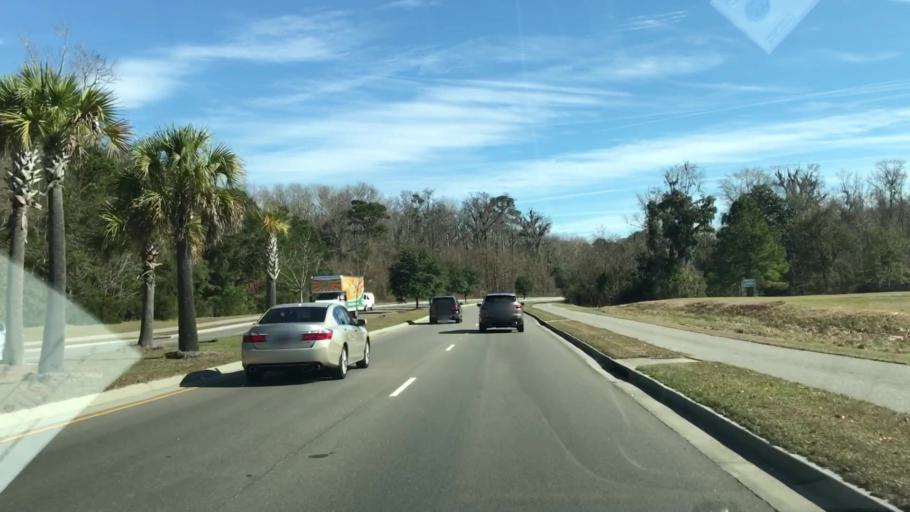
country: US
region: South Carolina
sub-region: Beaufort County
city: Bluffton
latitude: 32.2647
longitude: -80.8807
